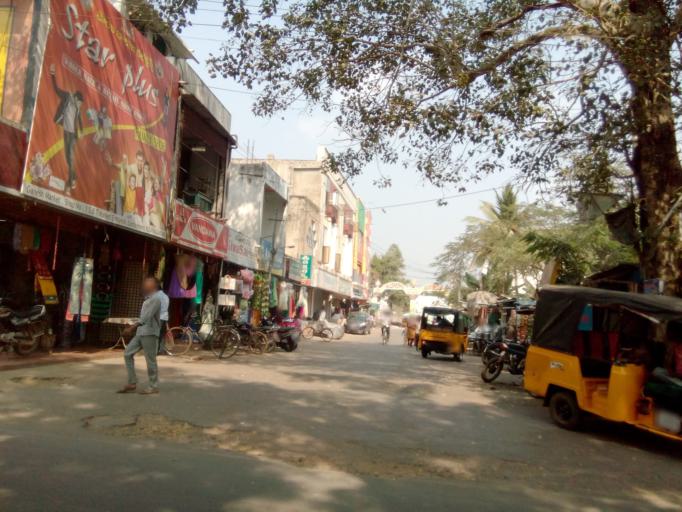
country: IN
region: Andhra Pradesh
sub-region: Vizianagaram District
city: Vizianagaram
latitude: 18.1174
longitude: 83.3934
